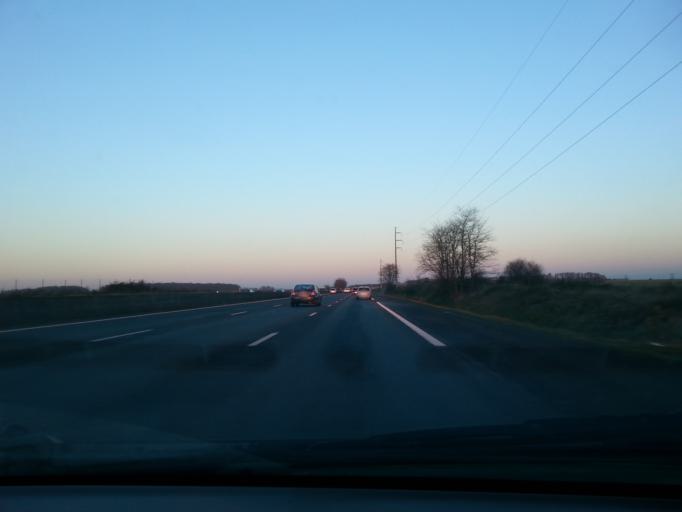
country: FR
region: Centre
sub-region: Departement d'Eure-et-Loir
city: Bailleau-le-Pin
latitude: 48.3051
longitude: 1.3001
